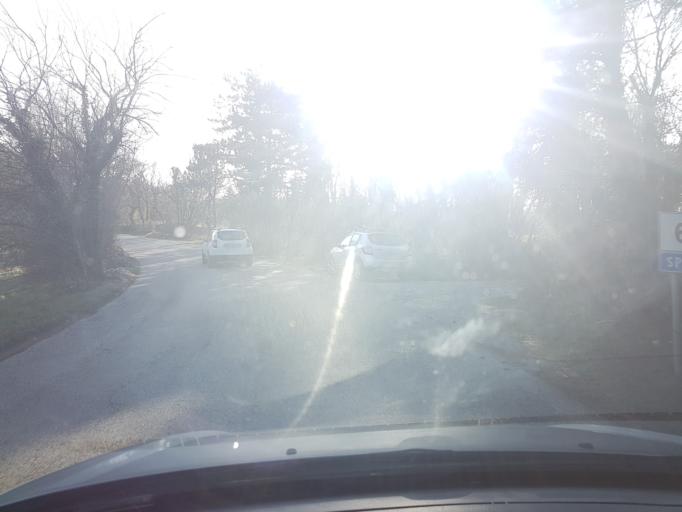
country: IT
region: Friuli Venezia Giulia
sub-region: Provincia di Trieste
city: Aurisina
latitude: 45.7709
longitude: 13.6872
